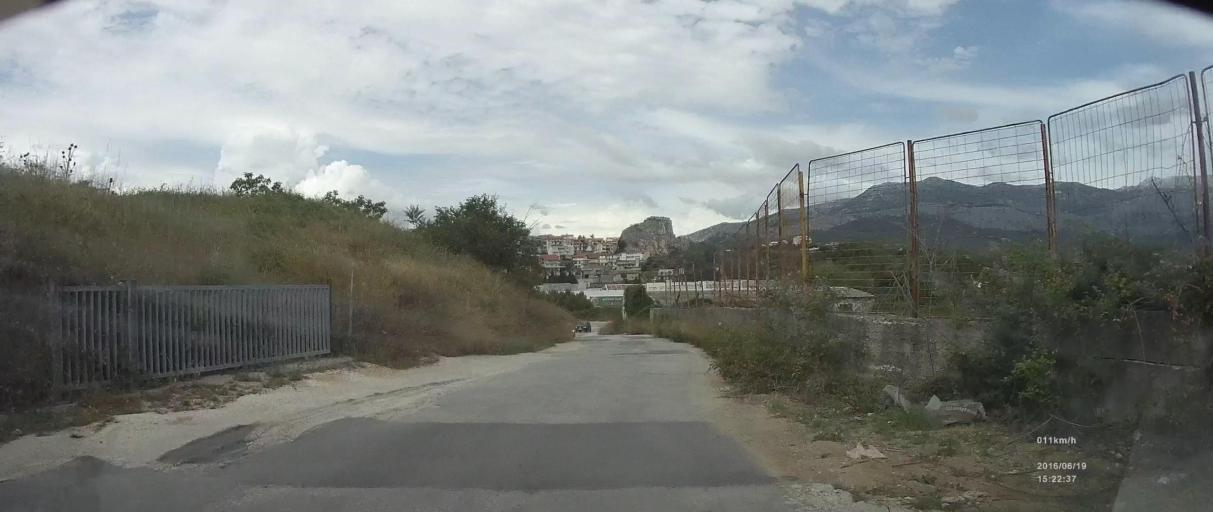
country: HR
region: Splitsko-Dalmatinska
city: Kamen
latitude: 43.5111
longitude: 16.5007
